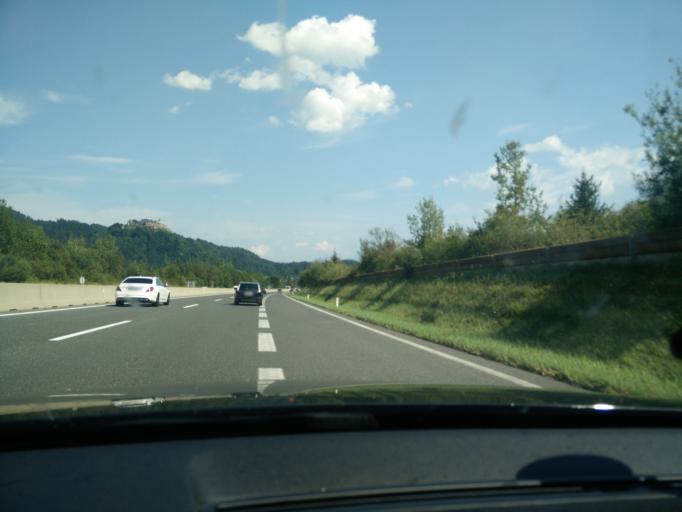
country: AT
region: Carinthia
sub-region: Villach Stadt
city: Villach
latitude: 46.6488
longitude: 13.8762
